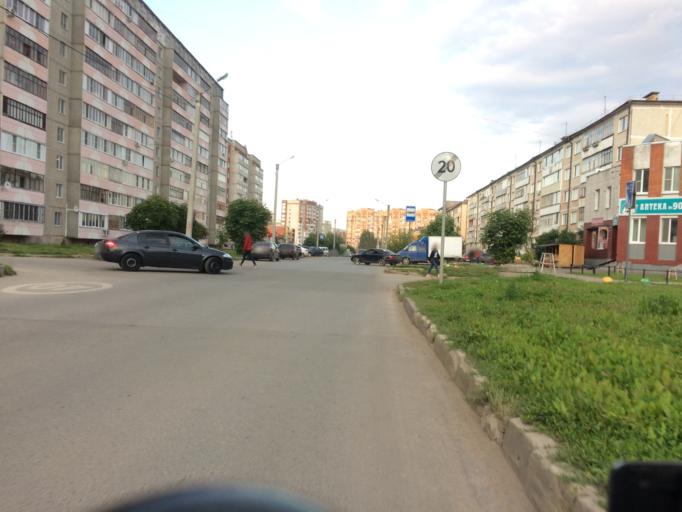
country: RU
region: Mariy-El
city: Medvedevo
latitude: 56.6446
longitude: 47.8408
